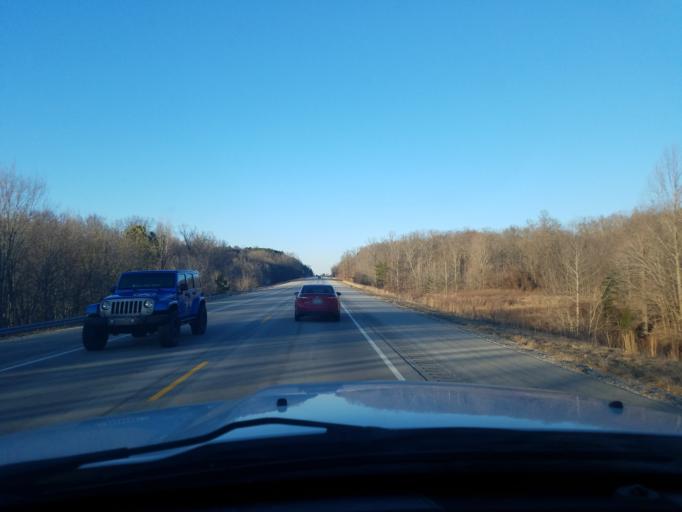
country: US
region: Indiana
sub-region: Crawford County
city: English
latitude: 38.1942
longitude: -86.5994
